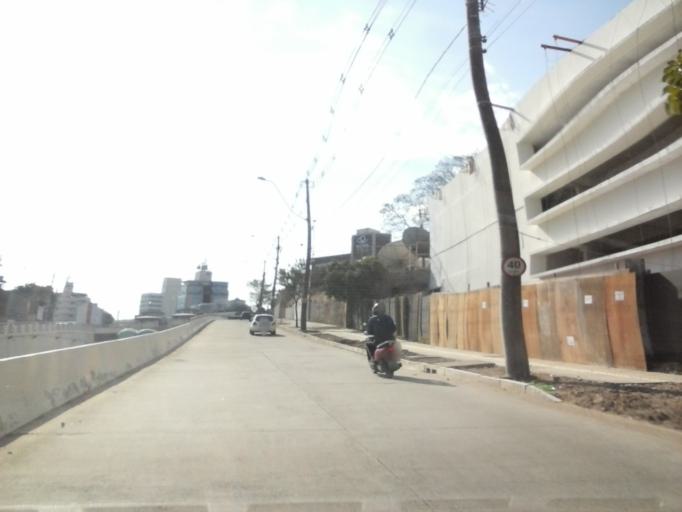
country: BR
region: Rio Grande do Sul
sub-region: Porto Alegre
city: Porto Alegre
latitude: -30.0407
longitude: -51.1731
